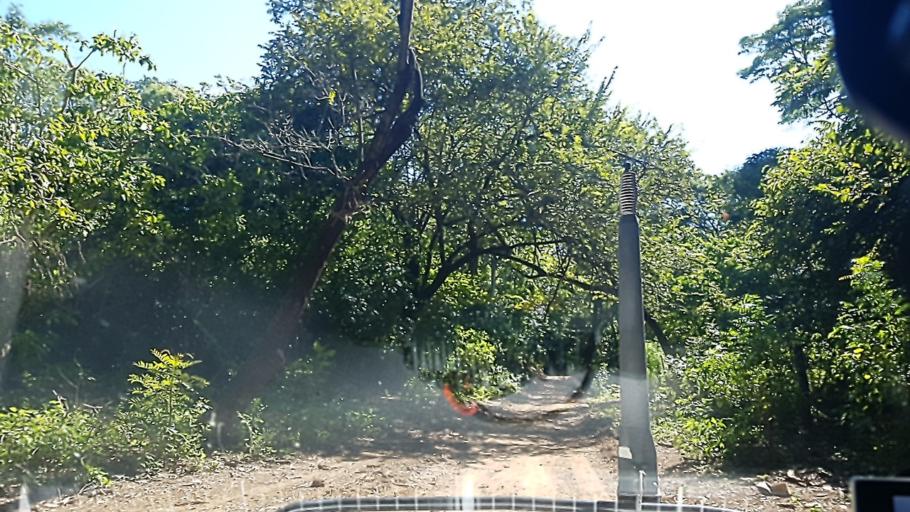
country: NI
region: Rivas
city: Tola
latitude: 11.5509
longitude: -86.0906
